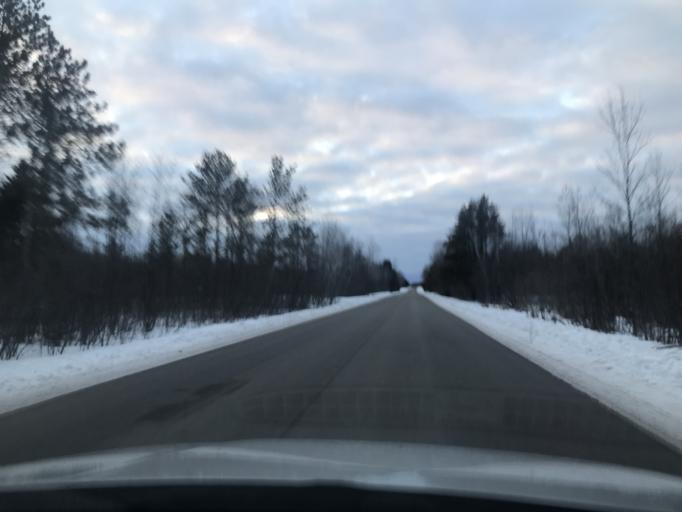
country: US
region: Wisconsin
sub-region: Marinette County
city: Peshtigo
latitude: 45.1646
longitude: -87.7462
